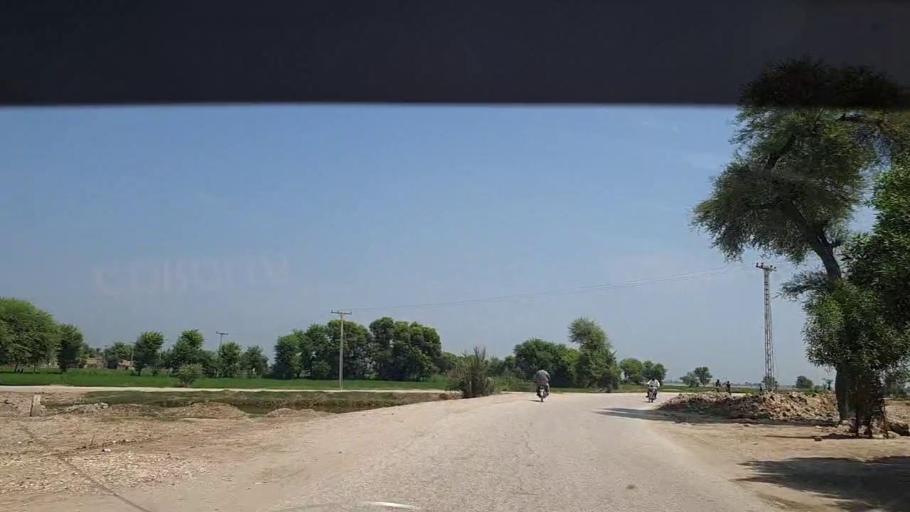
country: PK
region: Sindh
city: Rustam jo Goth
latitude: 28.0853
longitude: 68.7884
